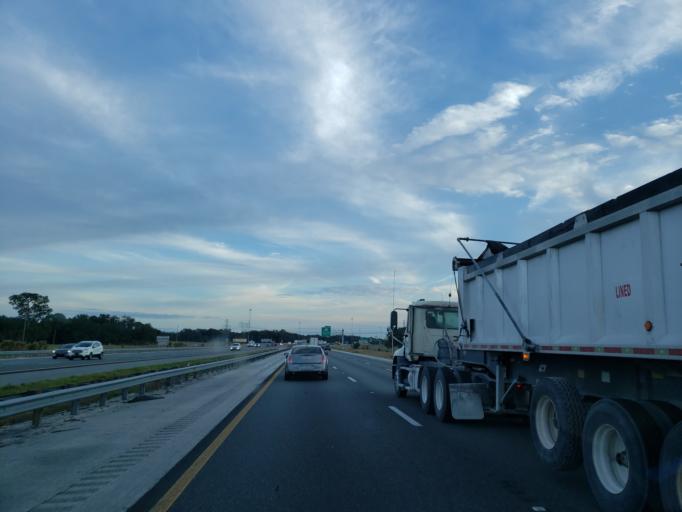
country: US
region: Florida
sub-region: Sumter County
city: Wildwood
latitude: 28.8873
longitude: -82.0970
